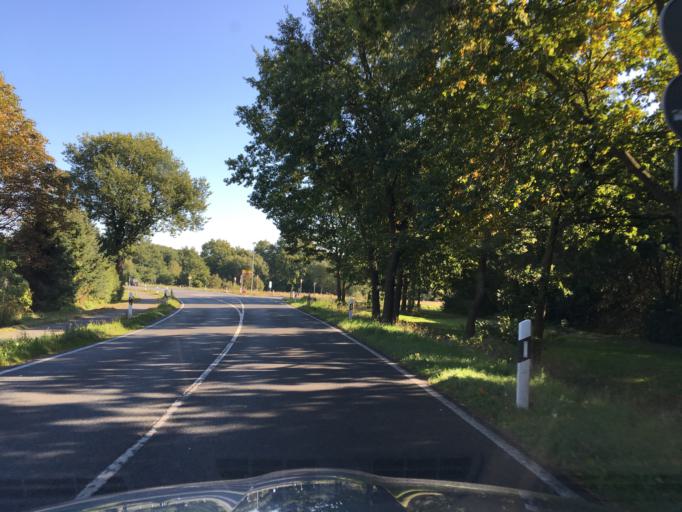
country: DE
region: Schleswig-Holstein
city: Lauenburg
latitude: 53.3637
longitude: 10.5526
